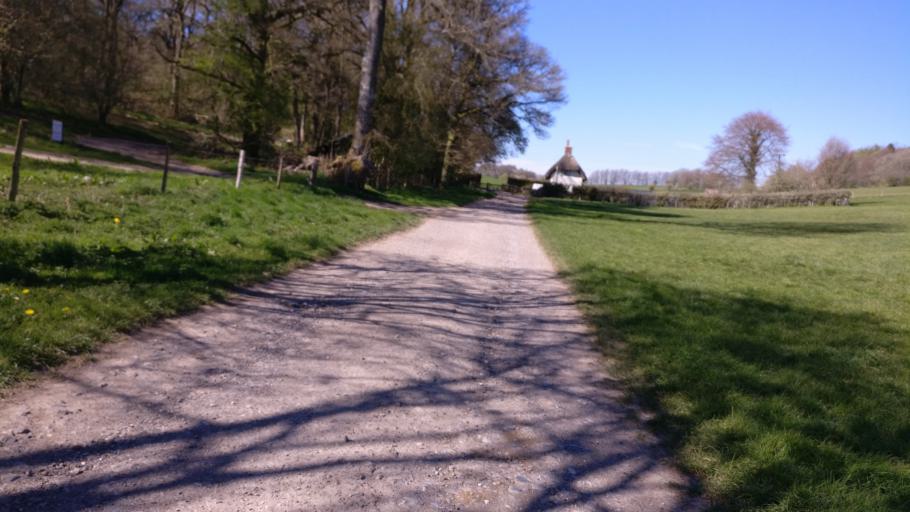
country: GB
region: England
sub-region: Hampshire
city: Basingstoke
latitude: 51.2113
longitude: -1.1052
